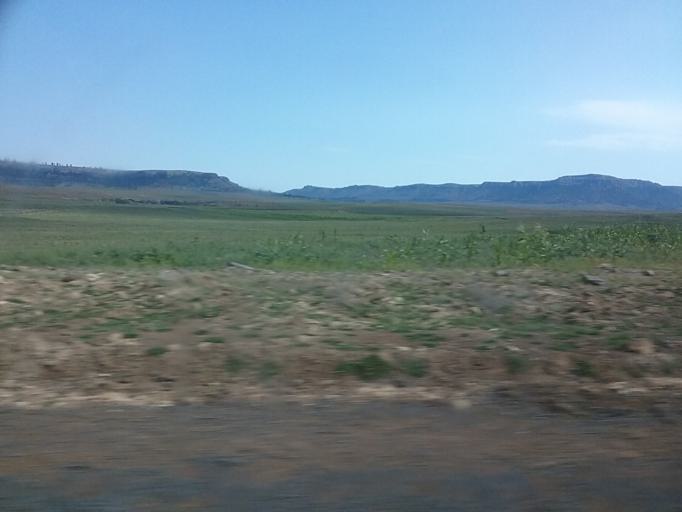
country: LS
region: Berea
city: Teyateyaneng
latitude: -29.0847
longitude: 27.8984
